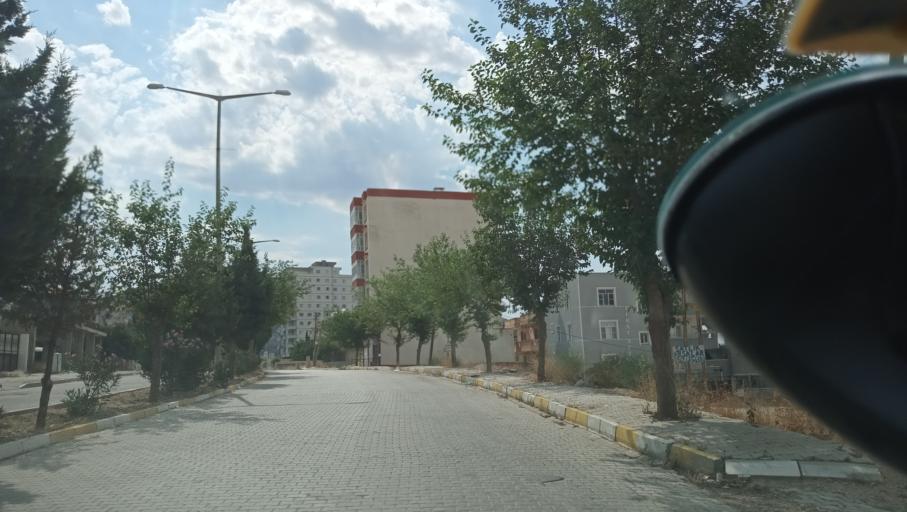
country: TR
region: Mardin
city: Kabala
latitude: 37.3407
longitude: 40.8114
